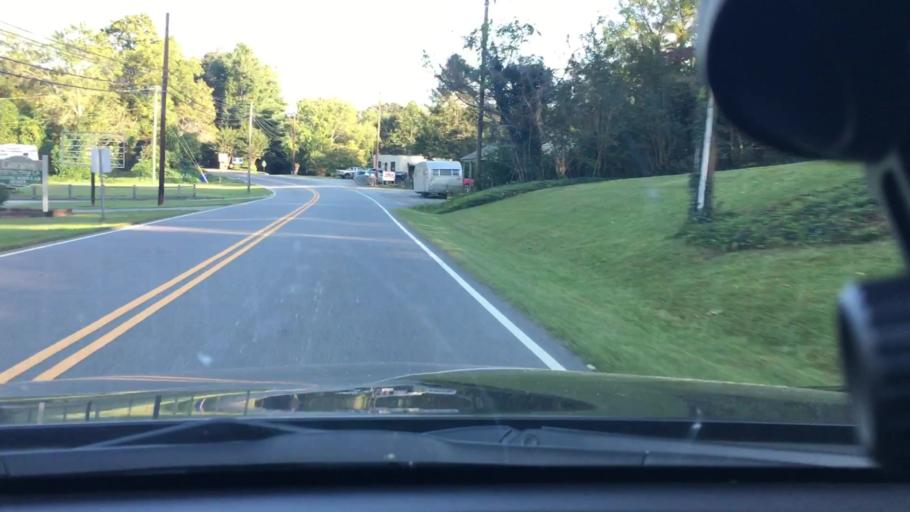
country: US
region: North Carolina
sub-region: Rutherford County
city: Rutherfordton
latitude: 35.3831
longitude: -81.9662
